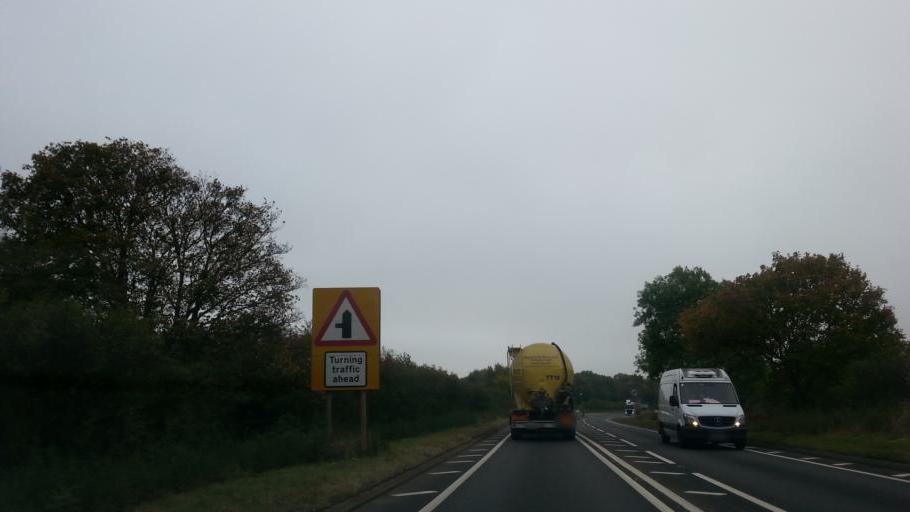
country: GB
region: England
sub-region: Northamptonshire
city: Oundle
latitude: 52.4545
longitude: -0.4626
